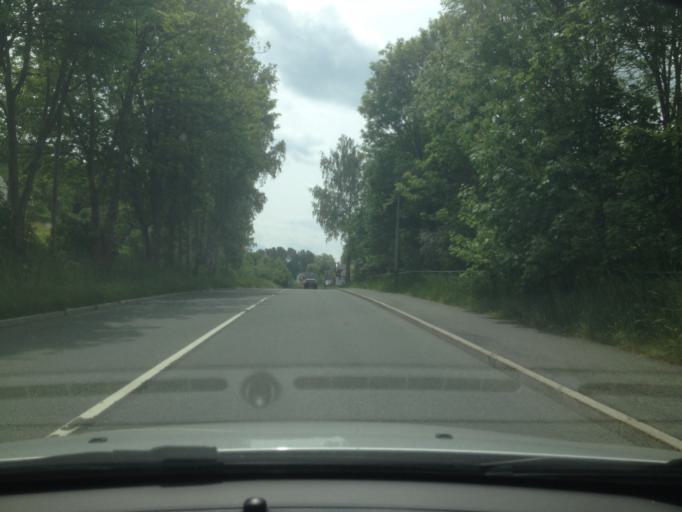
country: DE
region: Saxony
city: Stollberg
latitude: 50.6848
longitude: 12.7637
